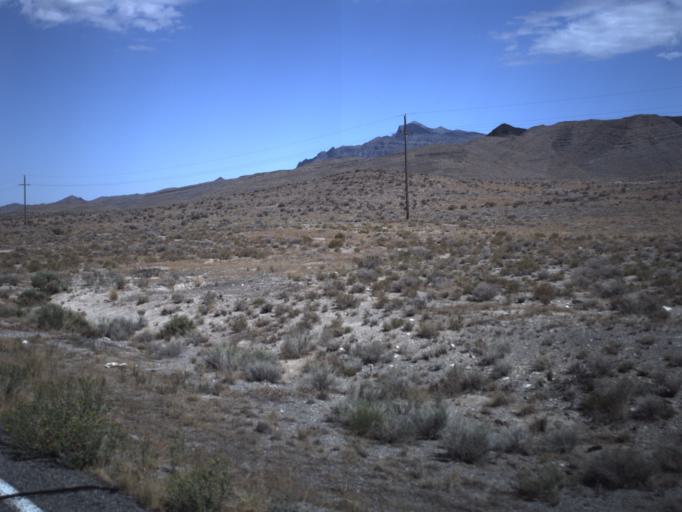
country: US
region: Utah
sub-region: Beaver County
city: Milford
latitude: 39.0241
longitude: -113.3697
